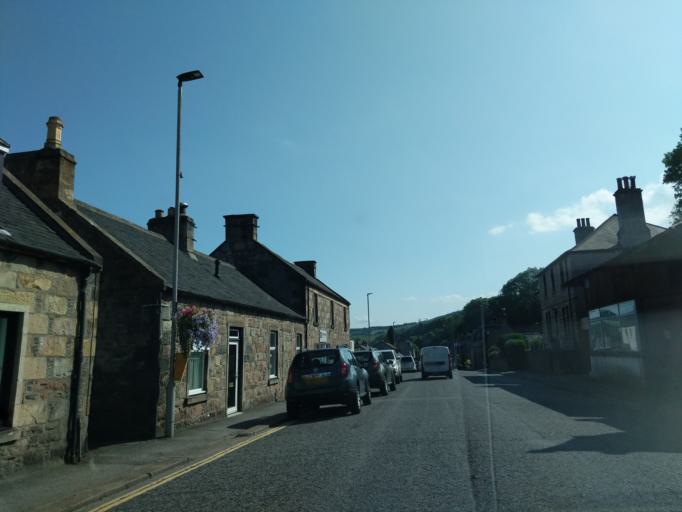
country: GB
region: Scotland
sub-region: Moray
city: Rothes
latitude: 57.5255
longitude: -3.2081
